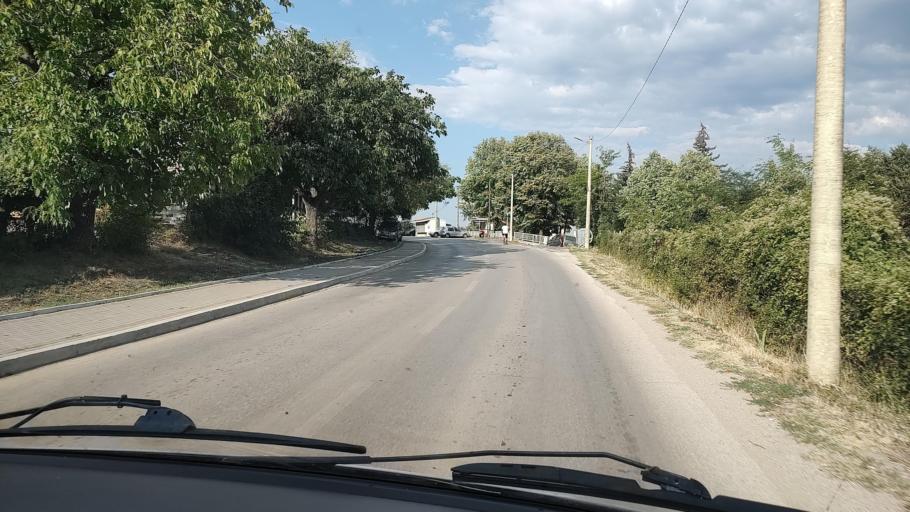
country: MK
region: Kriva Palanka
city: Kriva Palanka
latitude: 42.1942
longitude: 22.3149
